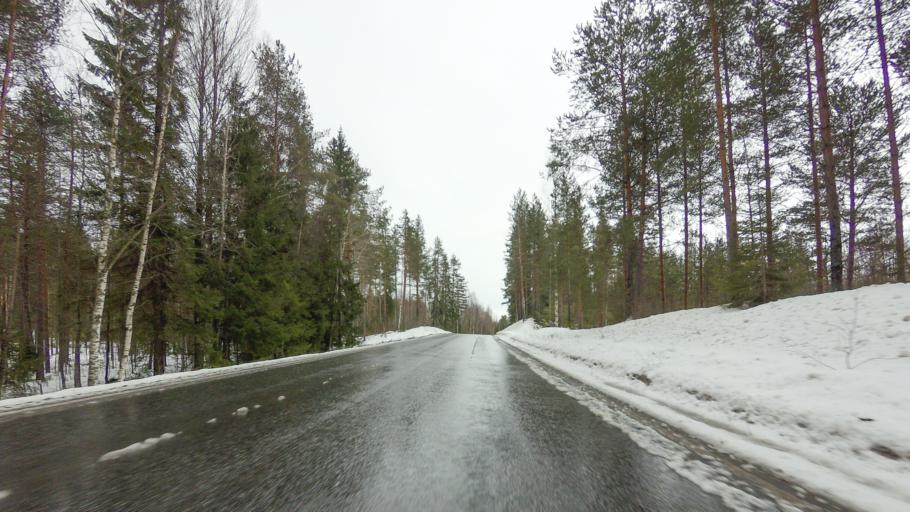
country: FI
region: Southern Savonia
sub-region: Savonlinna
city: Savonlinna
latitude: 61.9756
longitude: 28.8157
